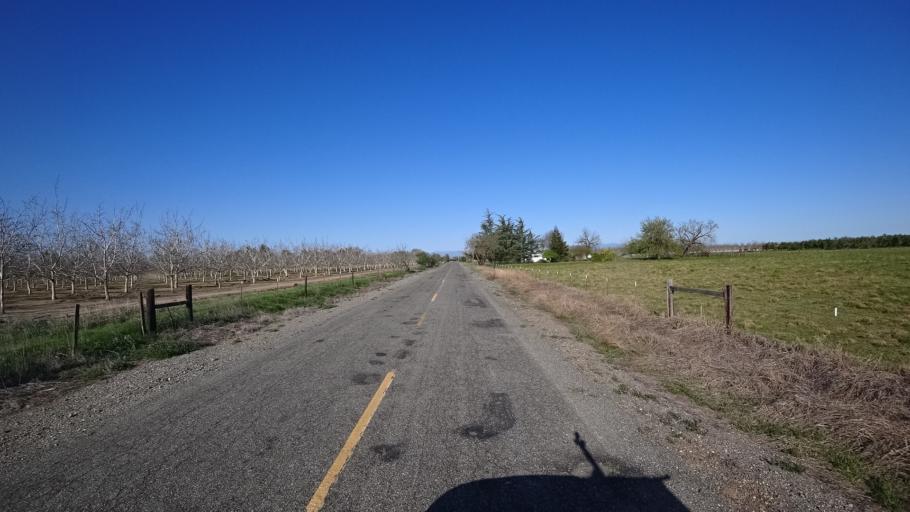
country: US
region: California
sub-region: Glenn County
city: Orland
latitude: 39.7574
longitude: -122.1249
